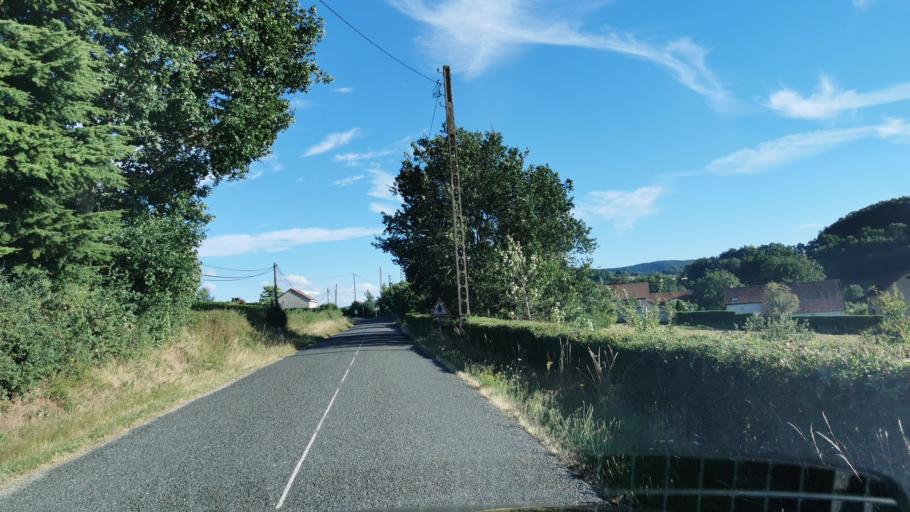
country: FR
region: Bourgogne
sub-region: Departement de Saone-et-Loire
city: Marmagne
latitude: 46.8232
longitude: 4.3231
